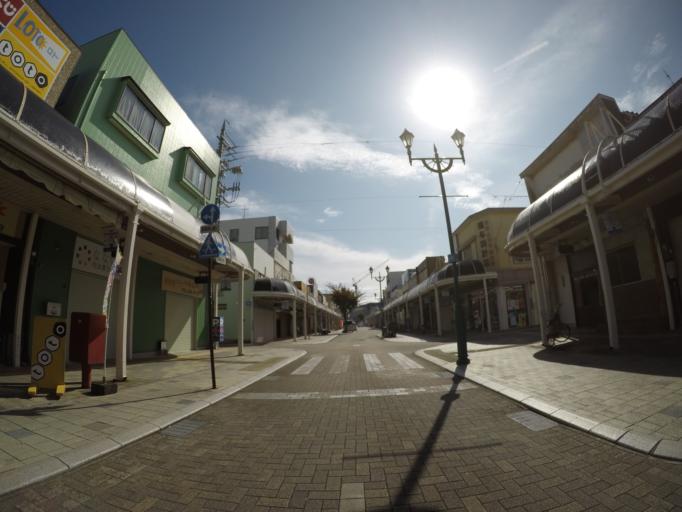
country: JP
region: Shizuoka
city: Yaizu
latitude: 34.8704
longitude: 138.3198
